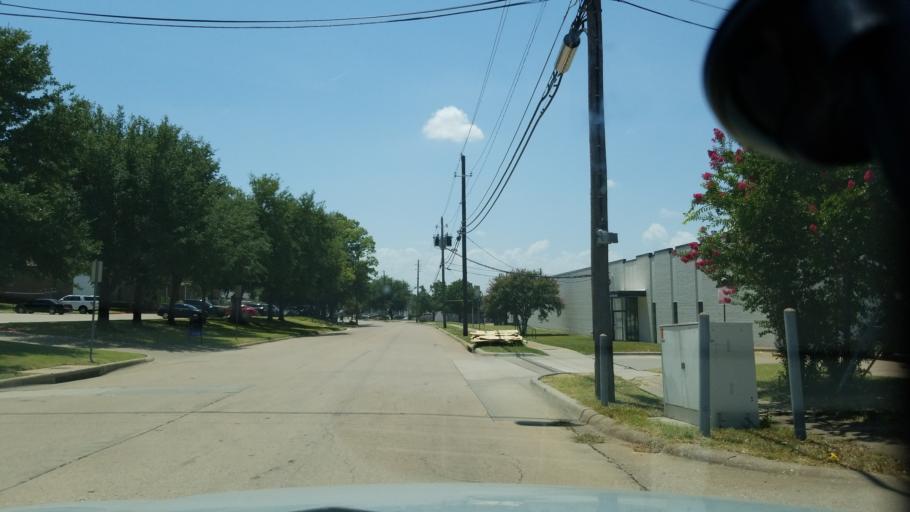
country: US
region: Texas
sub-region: Dallas County
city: Farmers Branch
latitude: 32.8943
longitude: -96.8846
